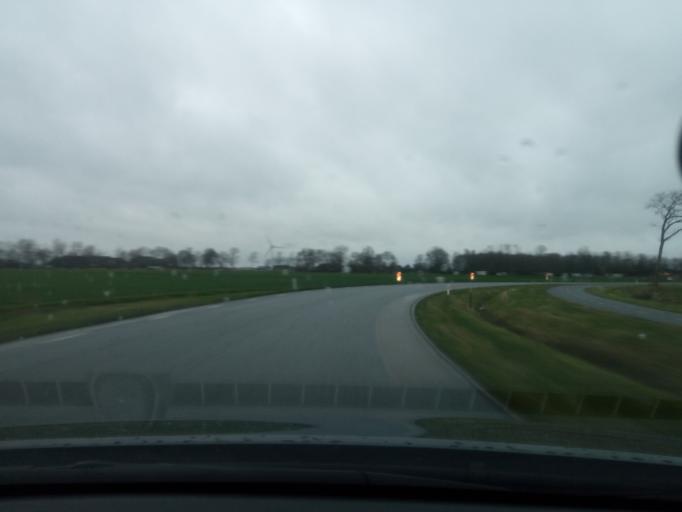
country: NL
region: Groningen
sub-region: Gemeente Bedum
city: Bedum
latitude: 53.3370
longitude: 6.5778
